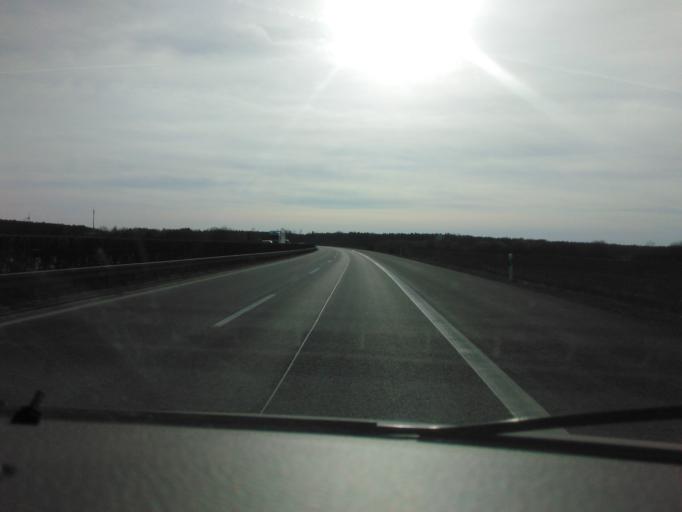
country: DE
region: Brandenburg
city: Grossraschen
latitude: 51.5870
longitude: 13.9388
